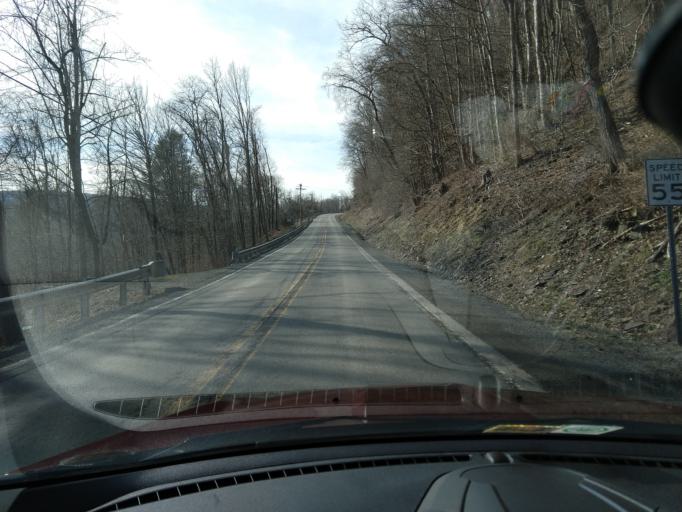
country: US
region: West Virginia
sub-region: Pocahontas County
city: Marlinton
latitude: 38.2195
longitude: -80.1015
